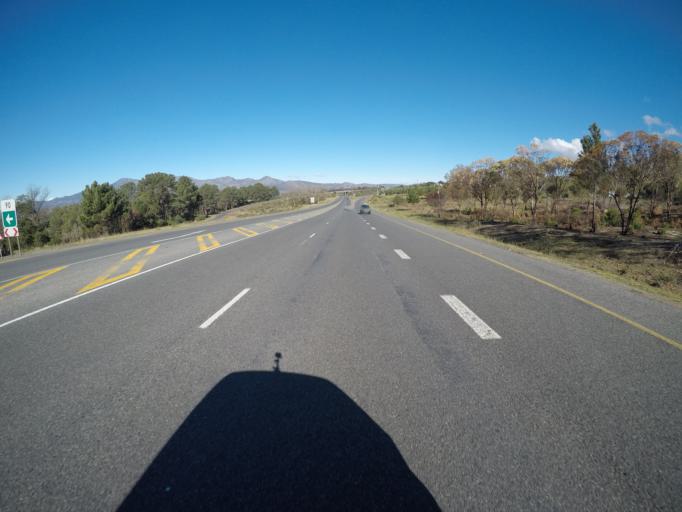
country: ZA
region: Western Cape
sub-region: Overberg District Municipality
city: Grabouw
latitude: -34.2259
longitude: 19.1877
